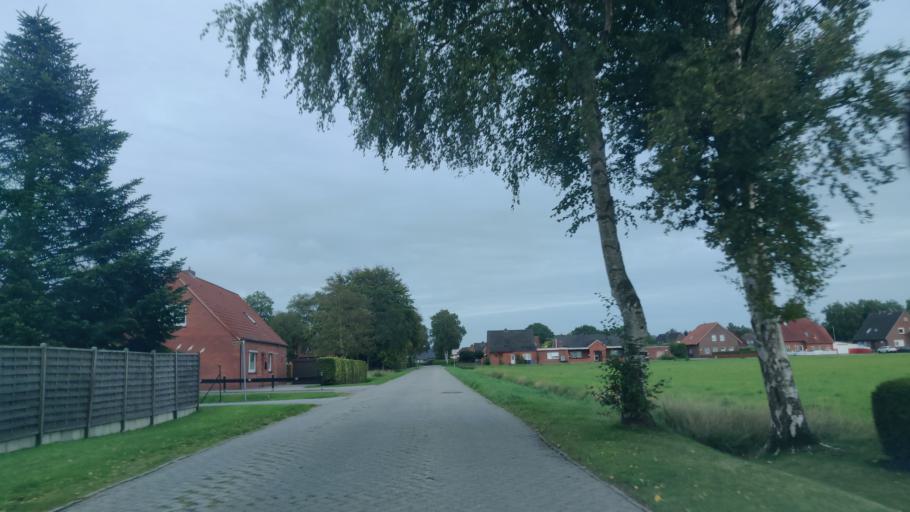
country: DE
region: Lower Saxony
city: Rechtsupweg
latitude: 53.4849
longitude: 7.3923
